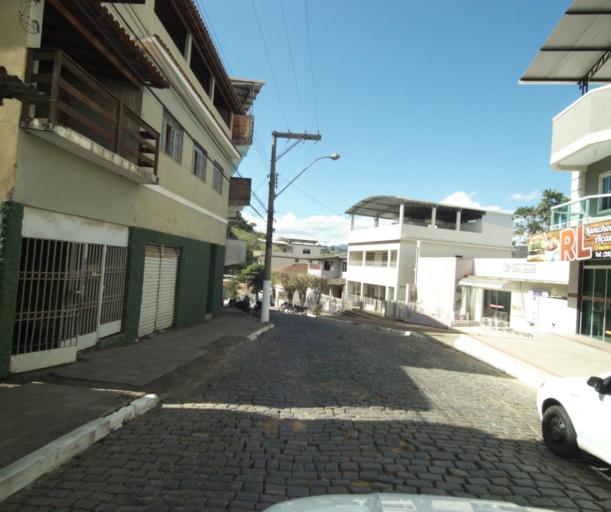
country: BR
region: Espirito Santo
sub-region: Sao Jose Do Calcado
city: Sao Jose do Calcado
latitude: -21.0259
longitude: -41.6532
